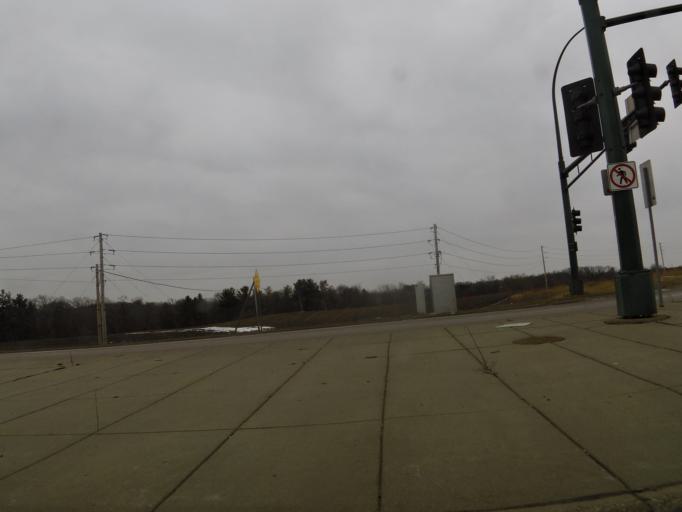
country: US
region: Minnesota
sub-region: Carver County
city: Chaska
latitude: 44.8059
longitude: -93.6238
